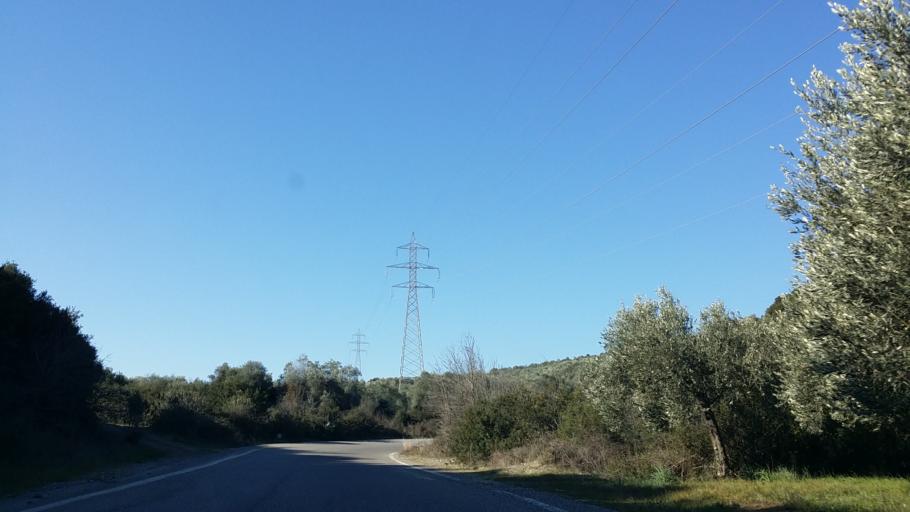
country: GR
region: West Greece
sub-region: Nomos Aitolias kai Akarnanias
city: Lepenou
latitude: 38.7444
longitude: 21.3451
